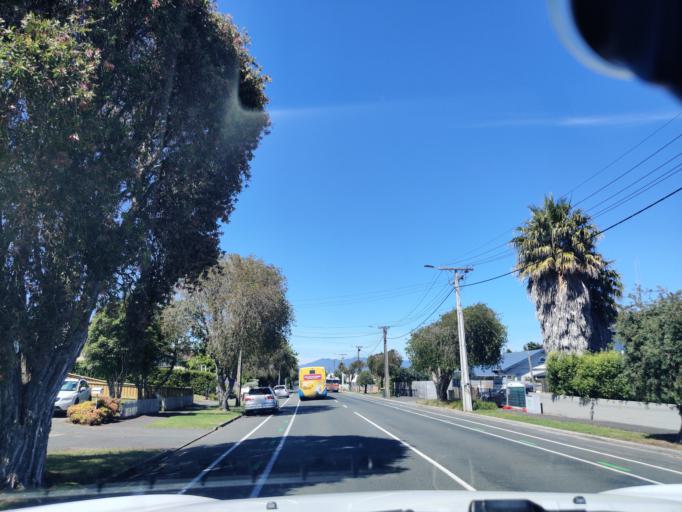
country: NZ
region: Waikato
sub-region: Hamilton City
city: Hamilton
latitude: -37.7913
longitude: 175.2689
